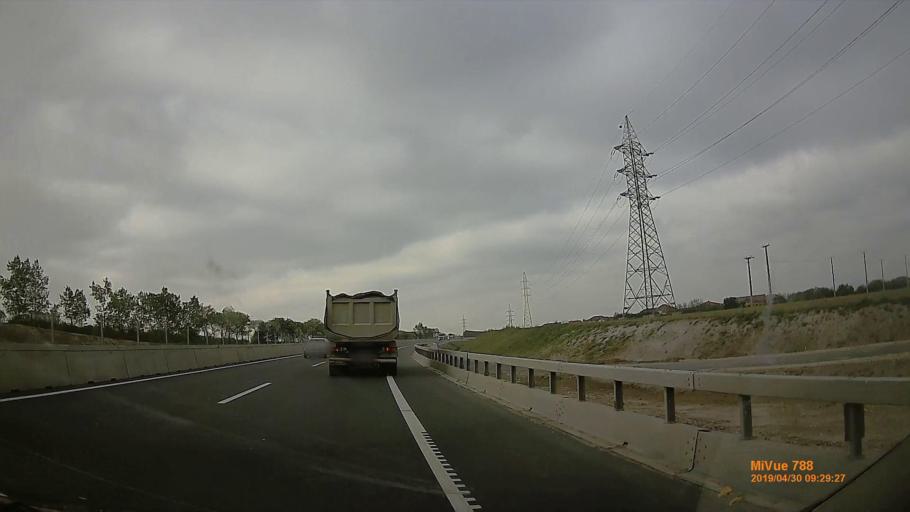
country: HU
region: Pest
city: Fot
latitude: 47.6343
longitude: 19.1695
